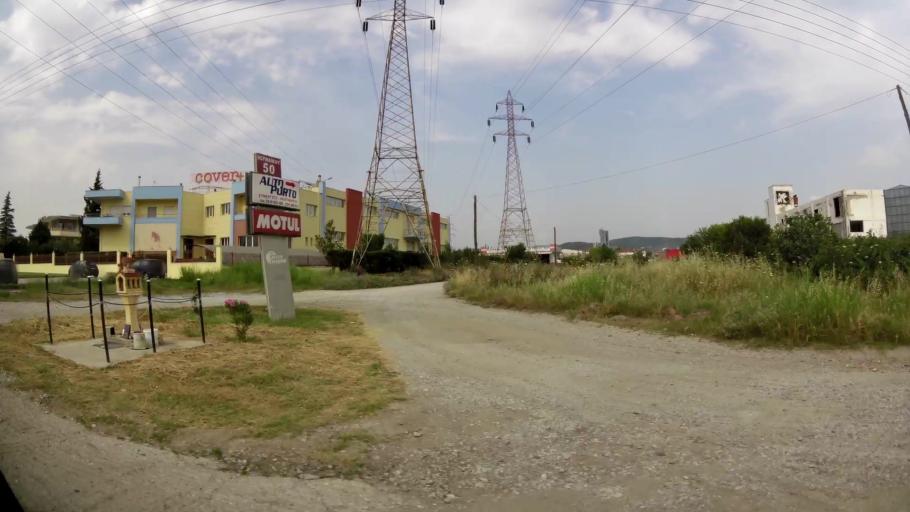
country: GR
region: Central Macedonia
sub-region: Nomos Thessalonikis
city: Efkarpia
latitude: 40.6964
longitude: 22.9321
